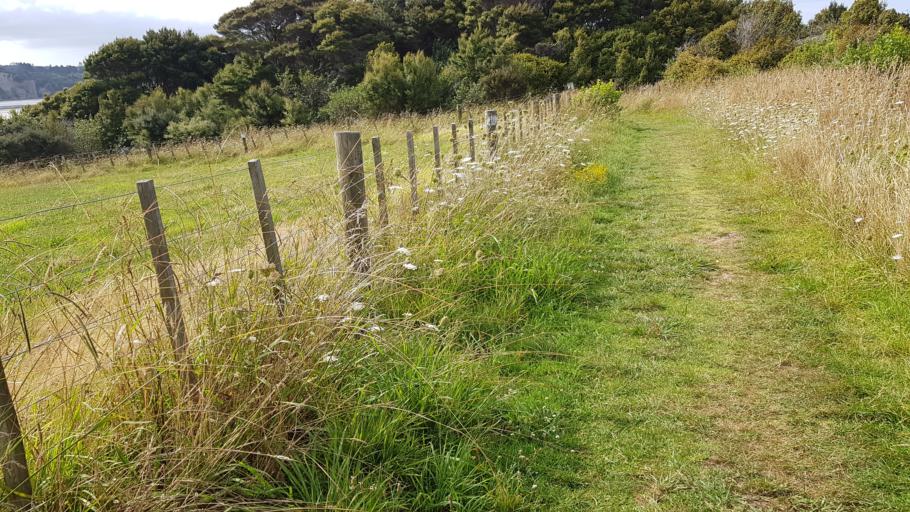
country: NZ
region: Auckland
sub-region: Auckland
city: Rothesay Bay
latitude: -36.6617
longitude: 174.7445
